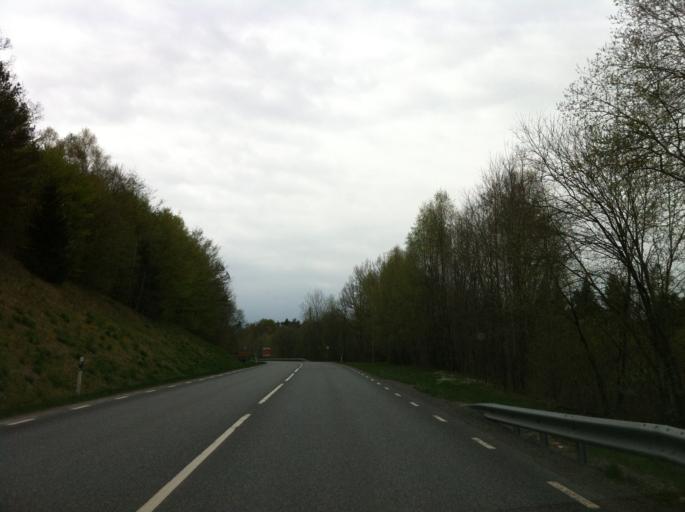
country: SE
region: Halland
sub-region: Falkenbergs Kommun
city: Falkenberg
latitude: 57.0936
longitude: 12.6749
